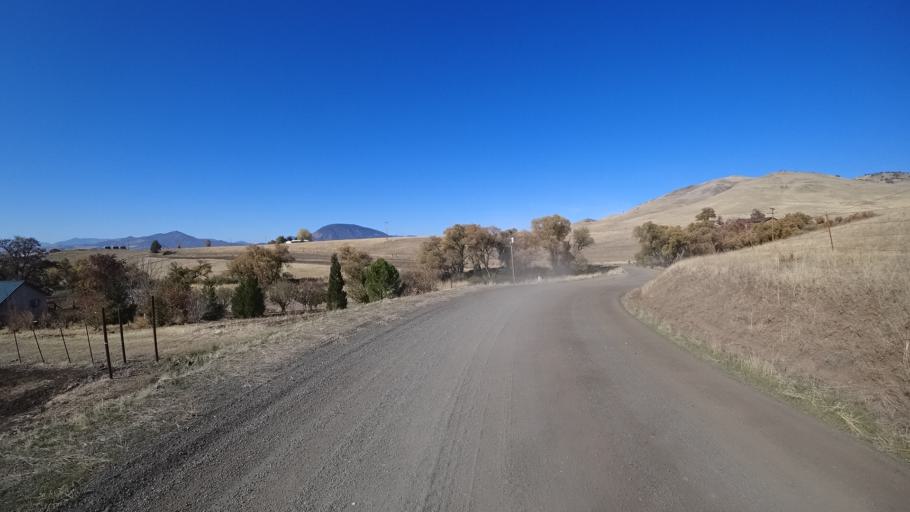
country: US
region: California
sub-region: Siskiyou County
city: Montague
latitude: 41.8311
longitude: -122.3874
